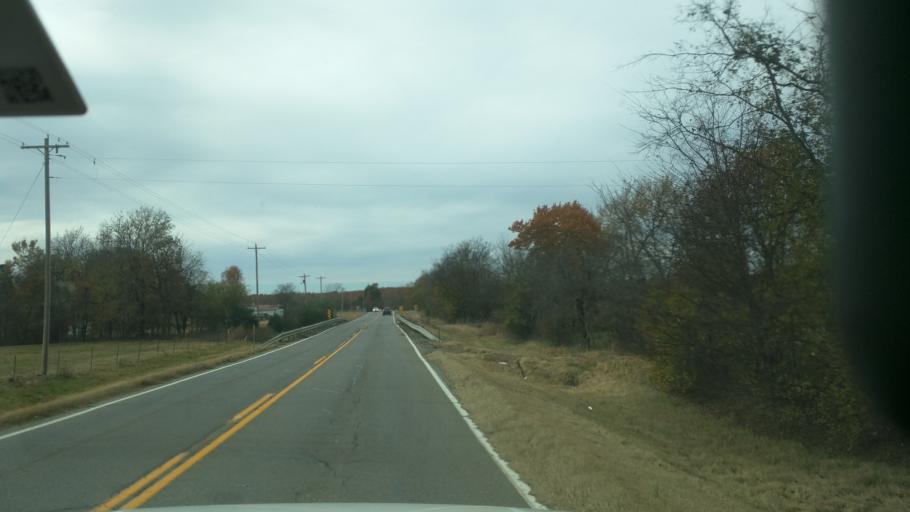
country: US
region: Oklahoma
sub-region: Cherokee County
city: Tahlequah
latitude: 35.9300
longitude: -94.8608
